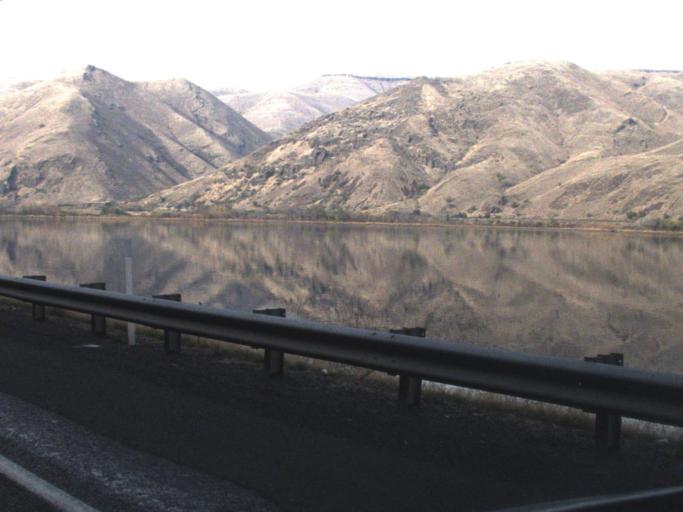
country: US
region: Washington
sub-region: Asotin County
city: Clarkston Heights-Vineland
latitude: 46.4238
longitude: -117.1264
